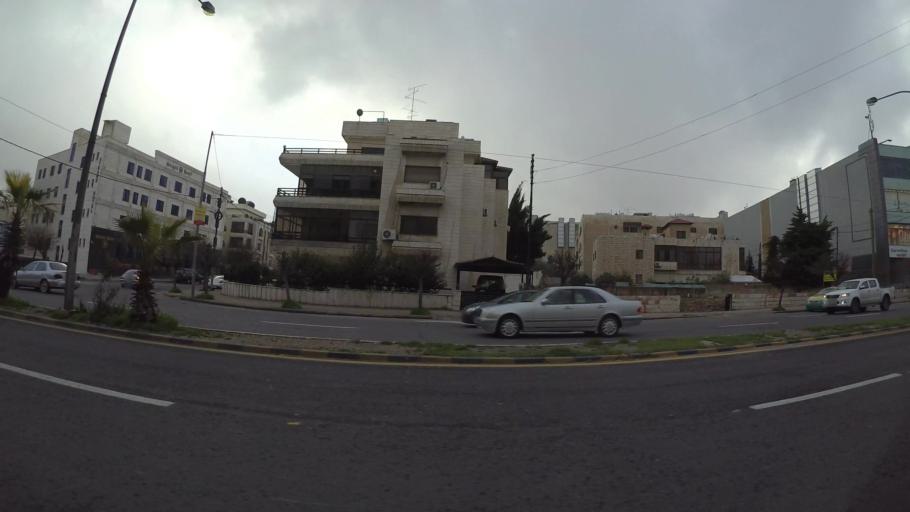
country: JO
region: Amman
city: Wadi as Sir
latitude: 31.9562
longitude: 35.8708
